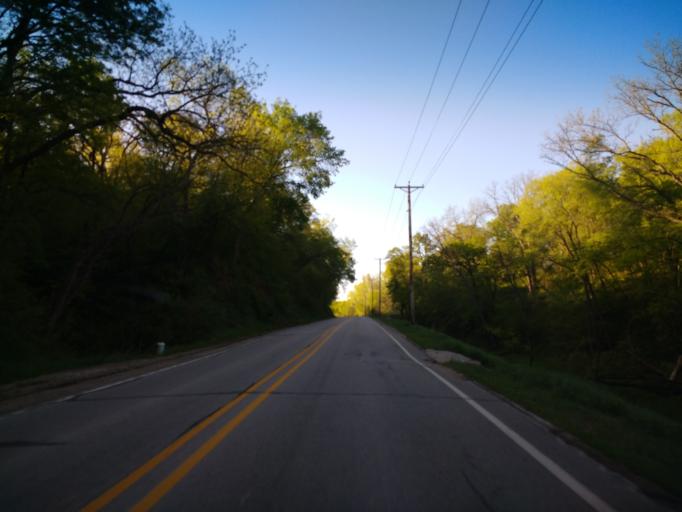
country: US
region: Iowa
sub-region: Harrison County
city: Missouri Valley
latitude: 41.4235
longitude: -95.8520
